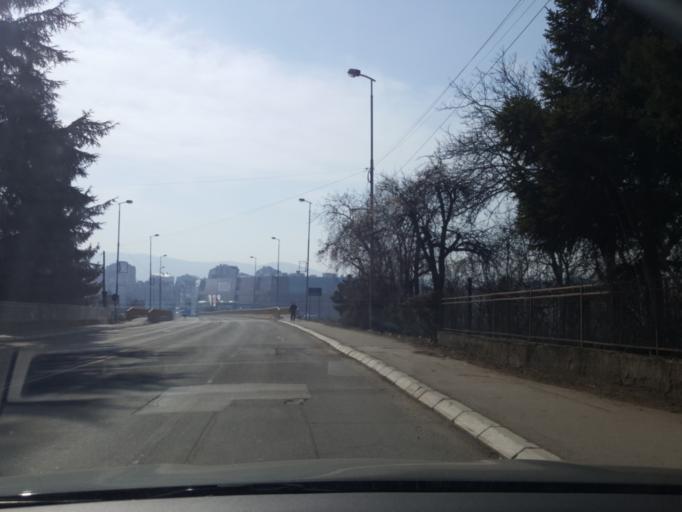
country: RS
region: Central Serbia
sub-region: Nisavski Okrug
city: Nis
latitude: 43.3268
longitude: 21.9253
